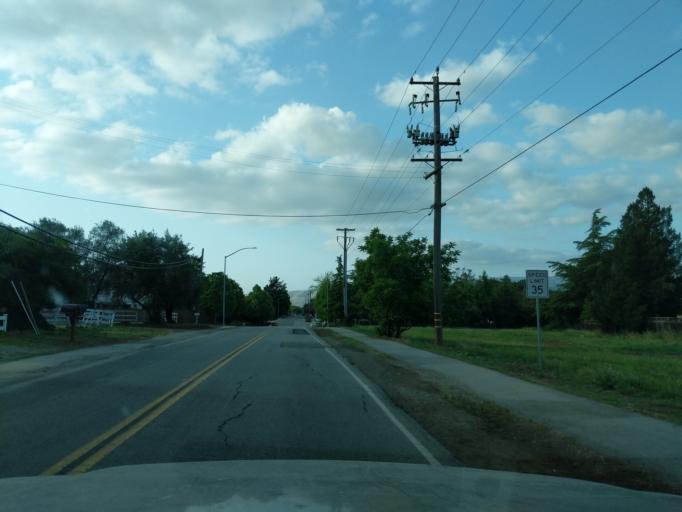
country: US
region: California
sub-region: Santa Clara County
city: Morgan Hill
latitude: 37.1172
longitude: -121.6617
